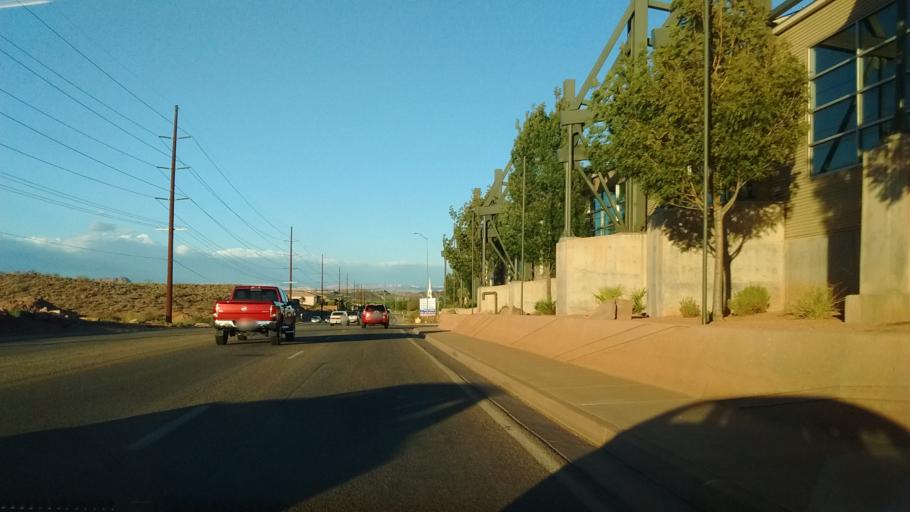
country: US
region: Utah
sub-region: Washington County
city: Washington
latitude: 37.1012
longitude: -113.5354
